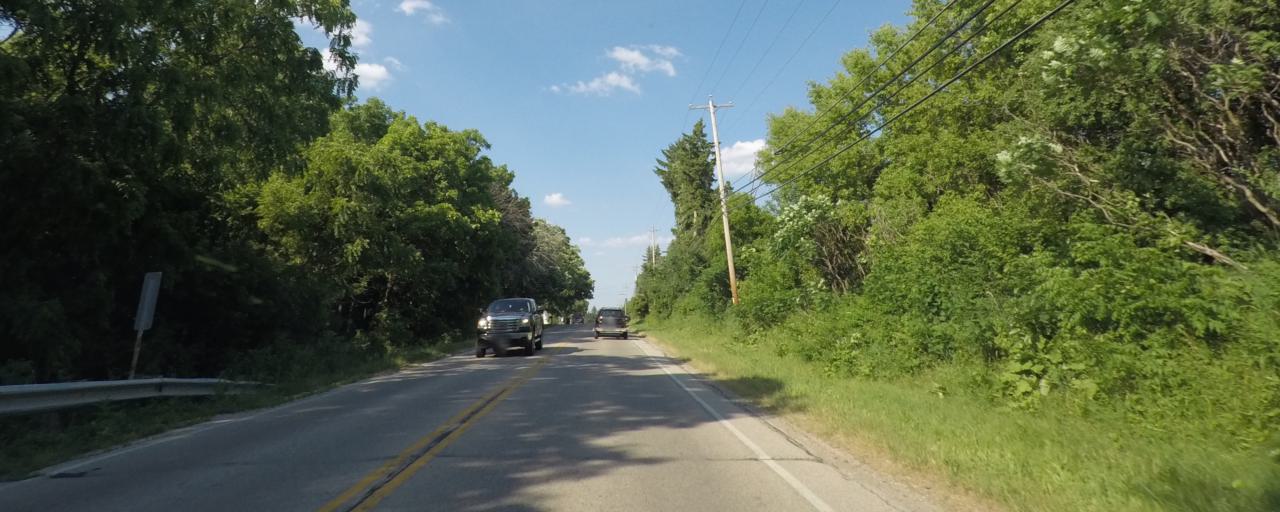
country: US
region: Wisconsin
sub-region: Waukesha County
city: Big Bend
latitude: 42.8650
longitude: -88.2278
